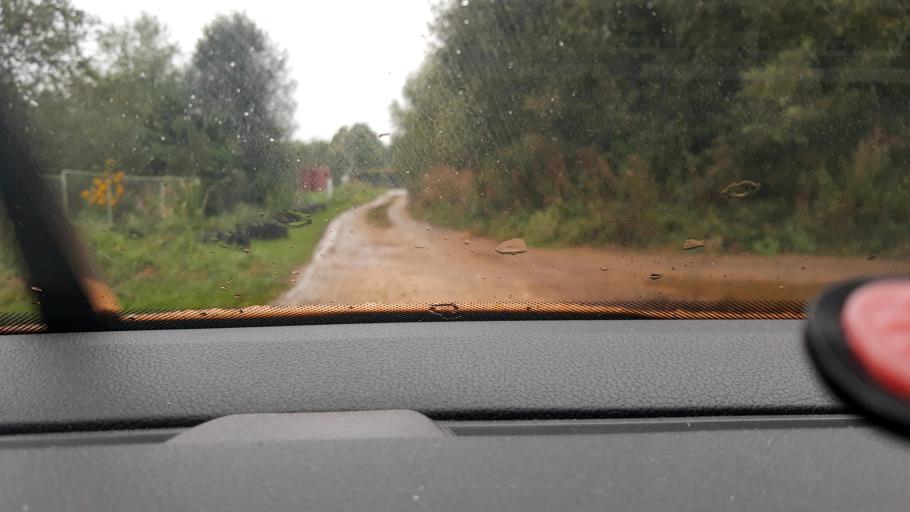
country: RU
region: Moskovskaya
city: Obukhovo
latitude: 55.8047
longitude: 38.2904
